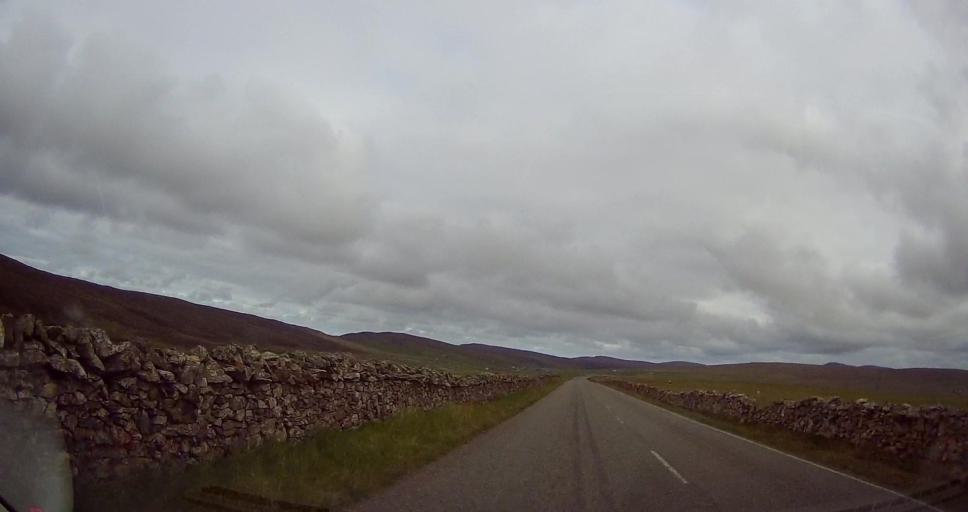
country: GB
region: Scotland
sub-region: Shetland Islands
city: Shetland
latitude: 60.7451
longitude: -0.8842
